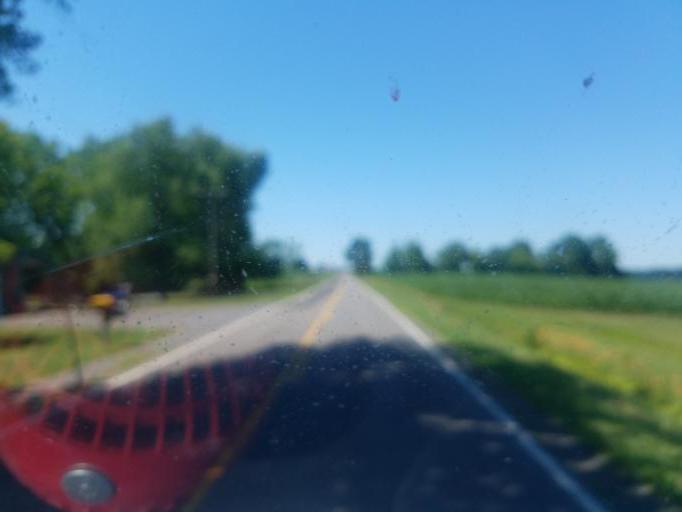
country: US
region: New York
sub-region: Ontario County
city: Geneva
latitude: 42.8145
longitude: -77.0341
